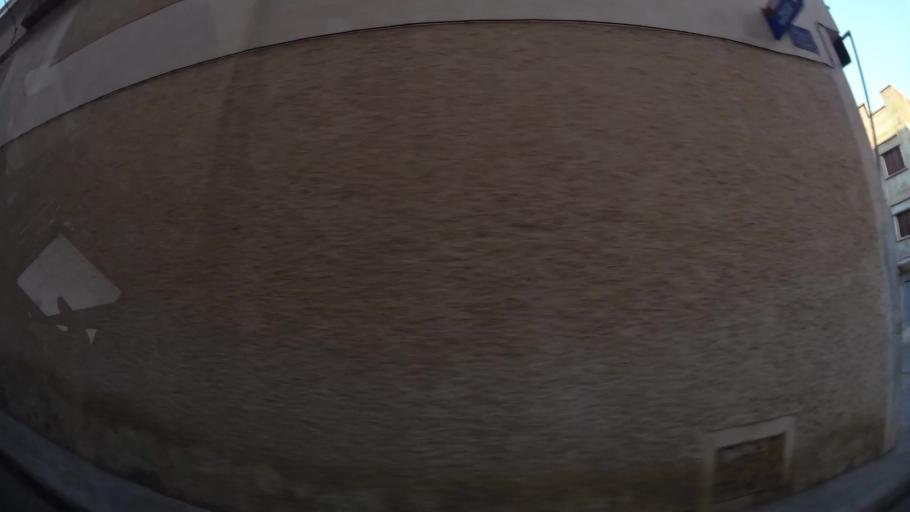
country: MA
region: Oriental
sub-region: Oujda-Angad
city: Oujda
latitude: 34.7064
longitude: -1.9135
